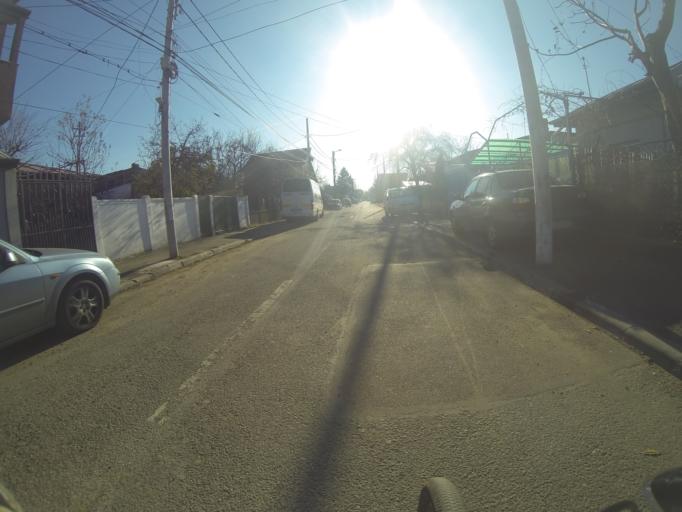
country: RO
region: Bucuresti
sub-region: Municipiul Bucuresti
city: Bucuresti
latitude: 44.3988
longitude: 26.0672
